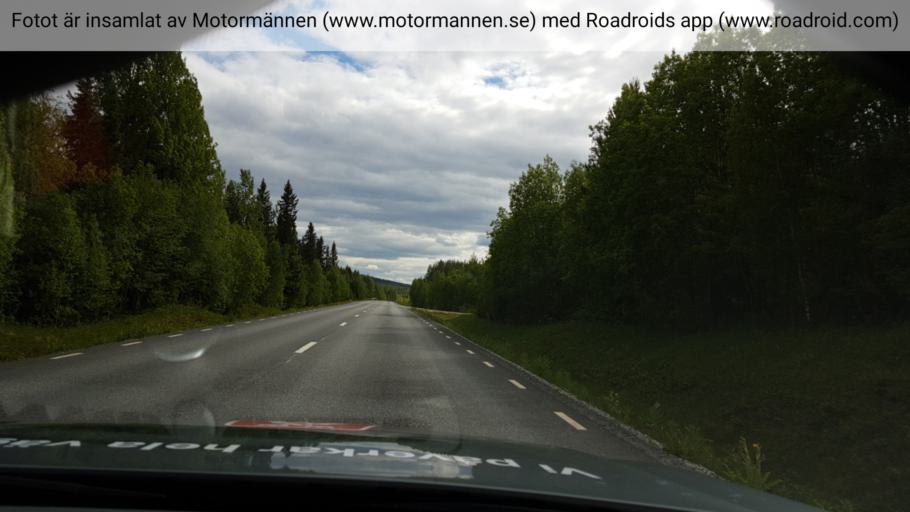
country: SE
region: Jaemtland
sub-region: Stroemsunds Kommun
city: Stroemsund
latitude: 64.0440
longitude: 15.5410
